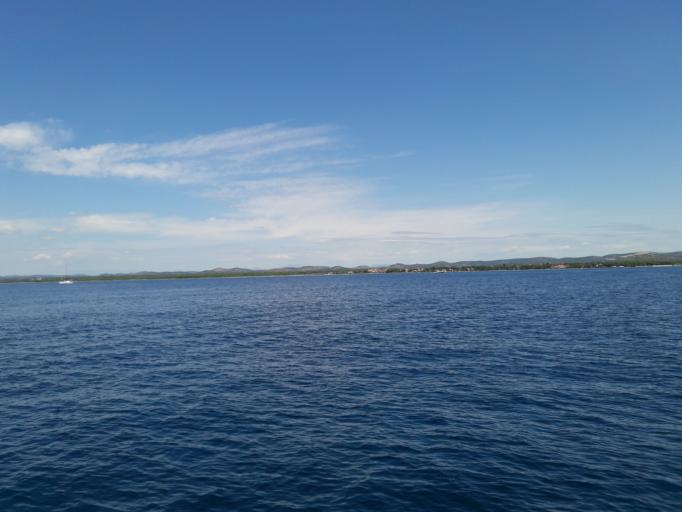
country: HR
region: Sibensko-Kniniska
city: Vodice
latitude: 43.7110
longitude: 15.8336
